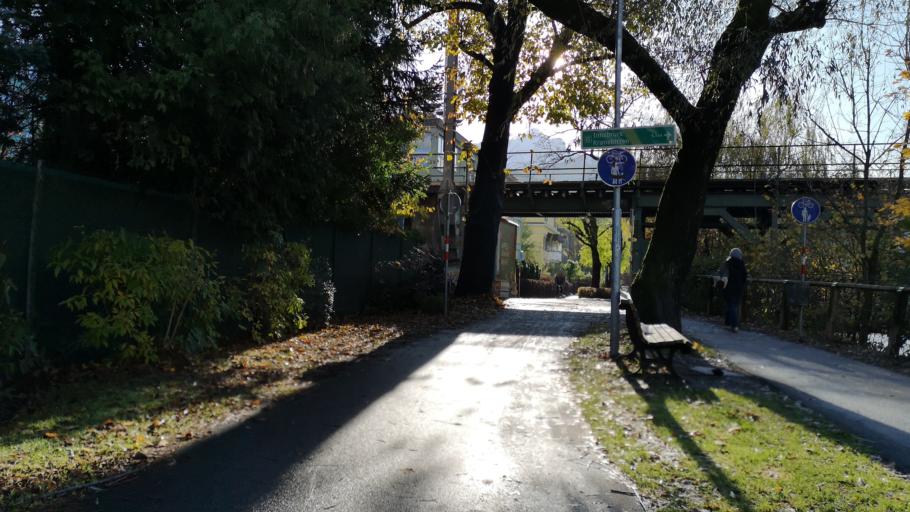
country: AT
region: Tyrol
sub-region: Innsbruck Stadt
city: Innsbruck
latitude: 47.2571
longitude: 11.3775
